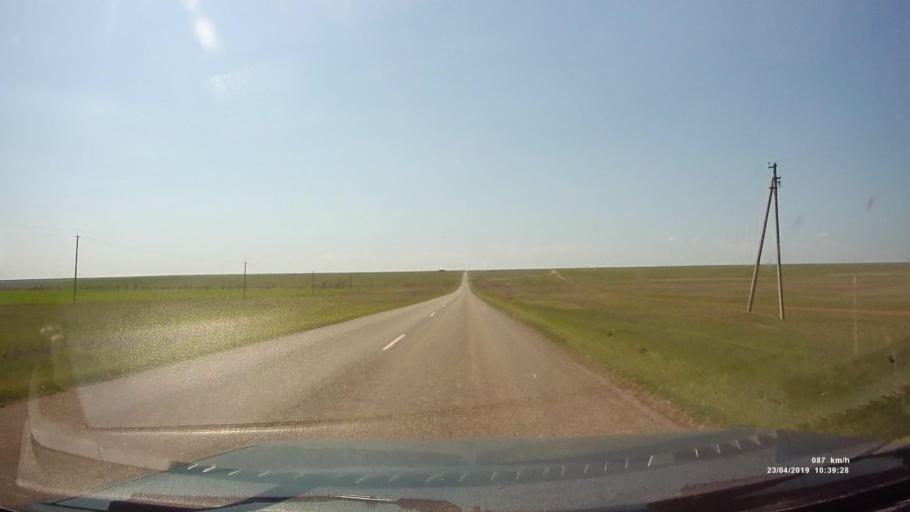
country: RU
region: Kalmykiya
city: Yashalta
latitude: 46.5189
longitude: 42.6387
